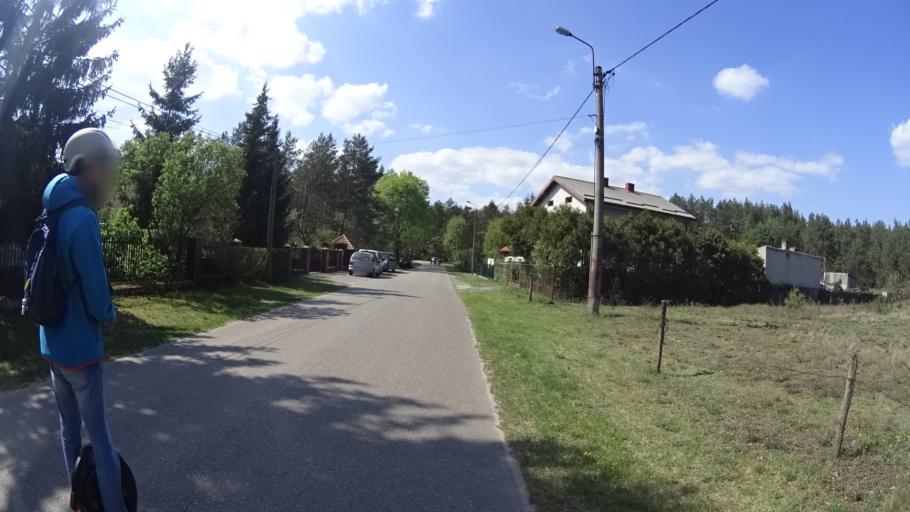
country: PL
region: Masovian Voivodeship
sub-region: Powiat warszawski zachodni
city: Truskaw
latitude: 52.3174
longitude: 20.7990
